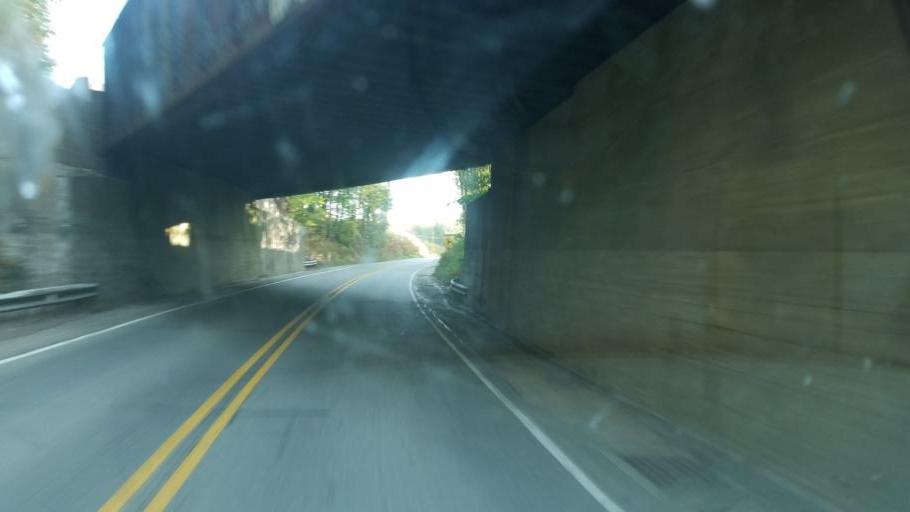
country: US
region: Pennsylvania
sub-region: Mercer County
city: Mercer
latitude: 41.3017
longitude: -80.2400
